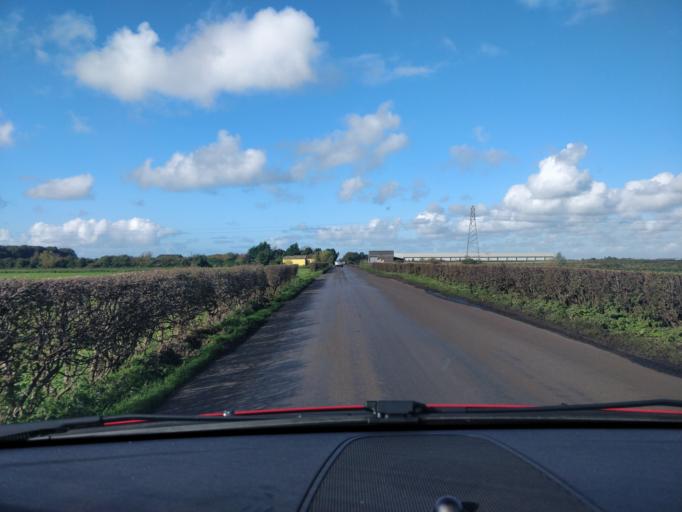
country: GB
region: England
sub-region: Lancashire
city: Tarleton
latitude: 53.6782
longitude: -2.8716
